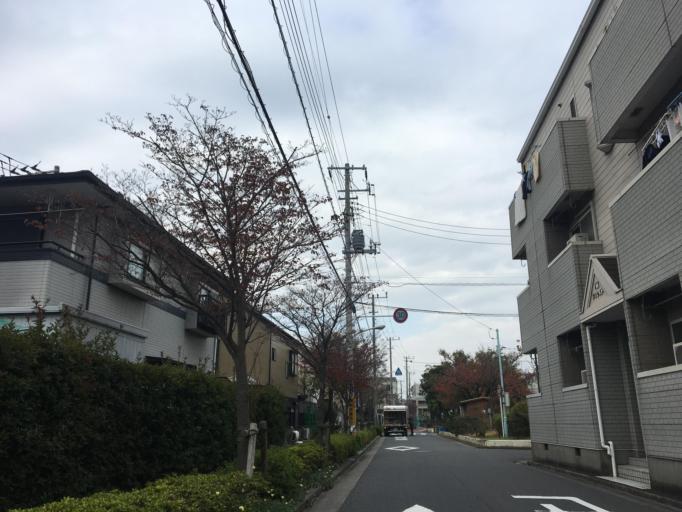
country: JP
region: Tokyo
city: Urayasu
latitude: 35.6567
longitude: 139.8846
